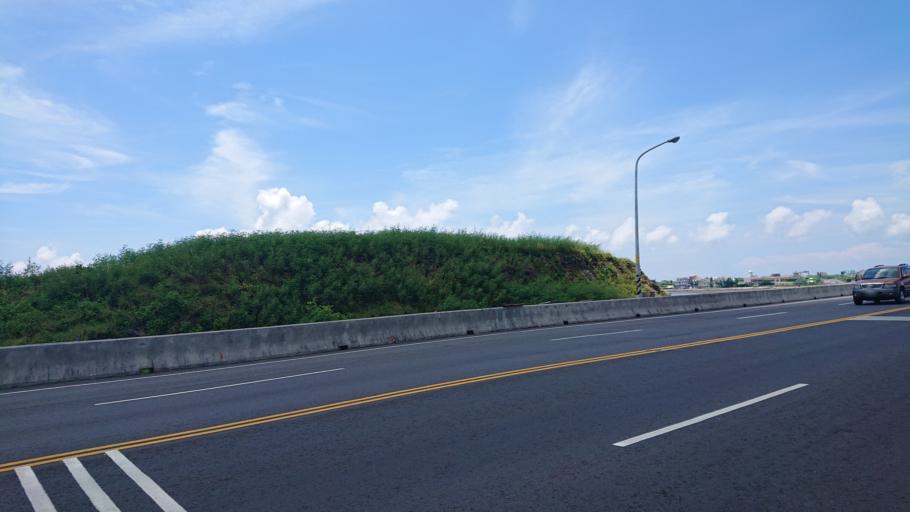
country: TW
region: Taiwan
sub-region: Penghu
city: Ma-kung
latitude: 23.6050
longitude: 119.6126
